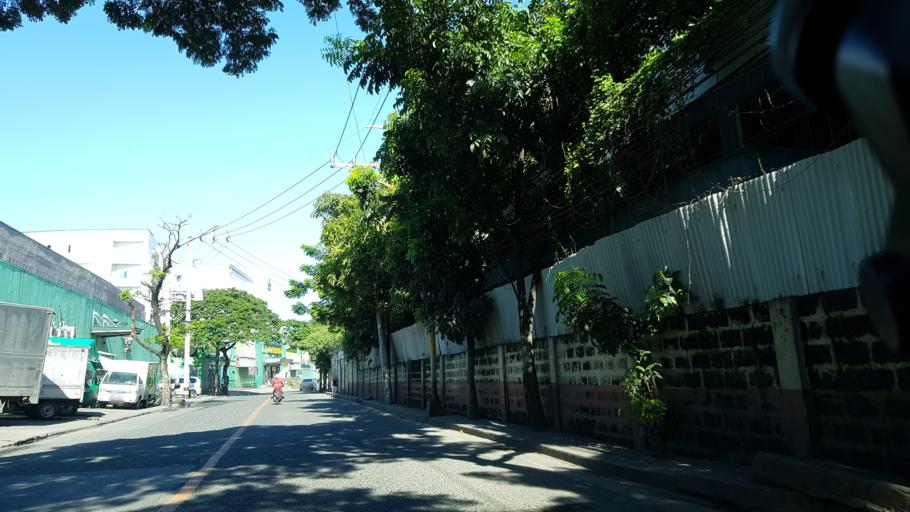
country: PH
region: Metro Manila
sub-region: Pasig
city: Pasig City
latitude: 14.5756
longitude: 121.0868
